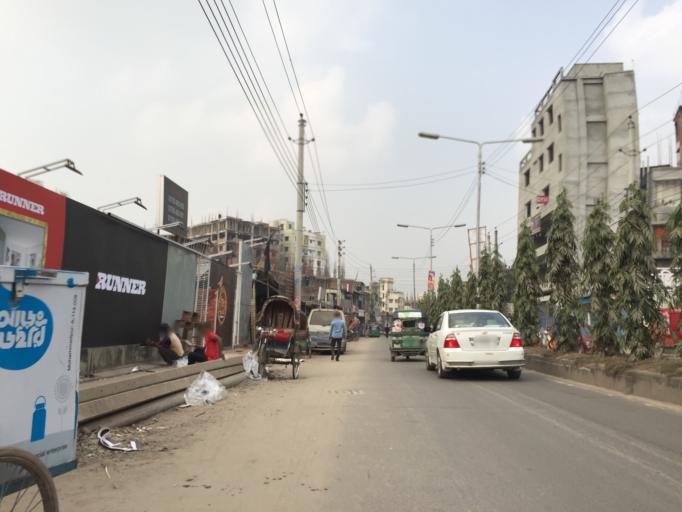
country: BD
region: Dhaka
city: Azimpur
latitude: 23.7838
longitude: 90.3680
